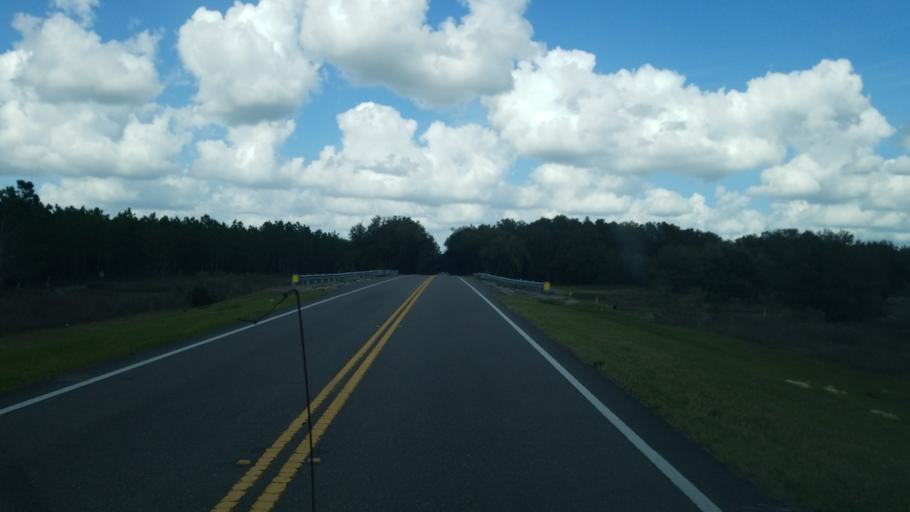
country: US
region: Florida
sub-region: Marion County
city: Belleview
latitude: 29.0521
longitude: -82.1527
